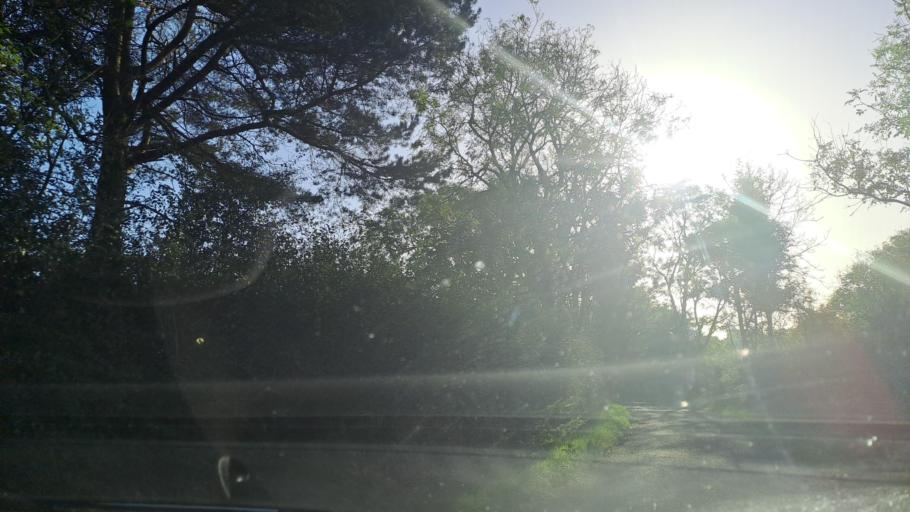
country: IE
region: Ulster
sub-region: An Cabhan
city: Kingscourt
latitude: 53.9802
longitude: -6.8513
